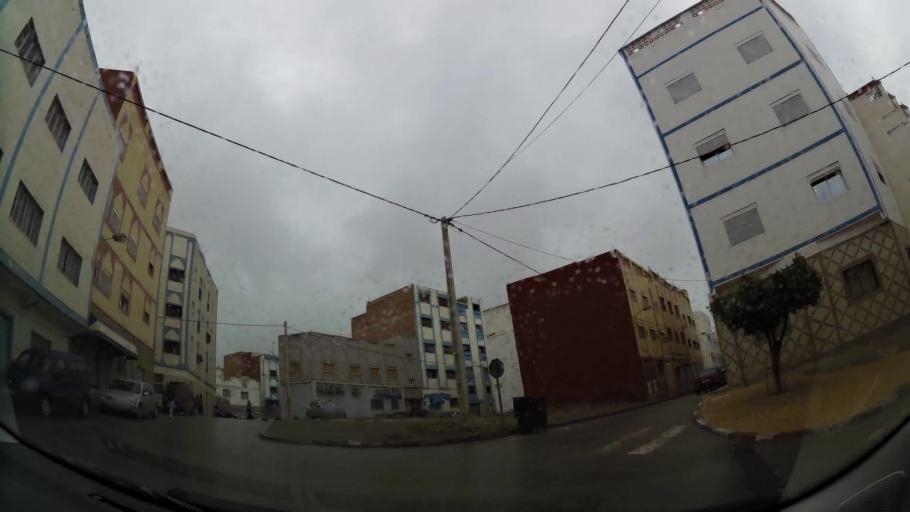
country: MA
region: Taza-Al Hoceima-Taounate
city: Imzourene
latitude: 35.1430
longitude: -3.8518
